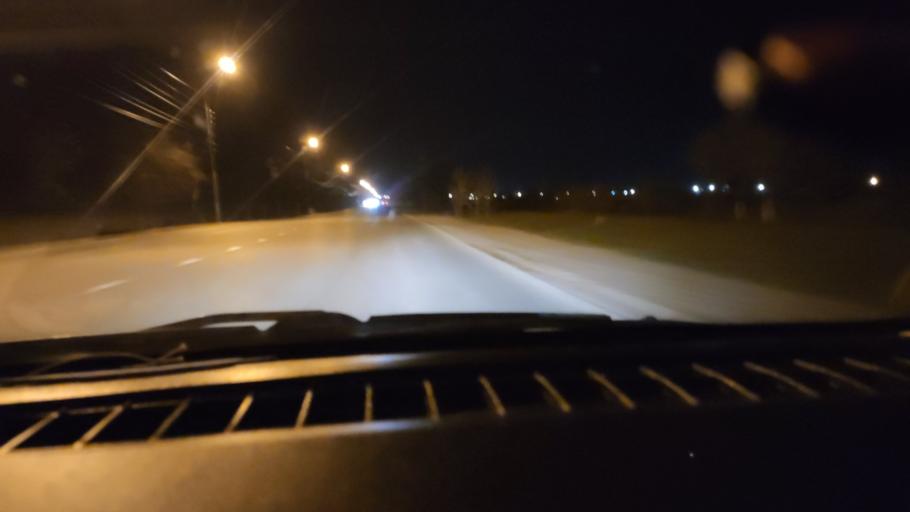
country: RU
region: Saratov
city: Privolzhskiy
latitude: 51.4365
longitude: 46.0619
